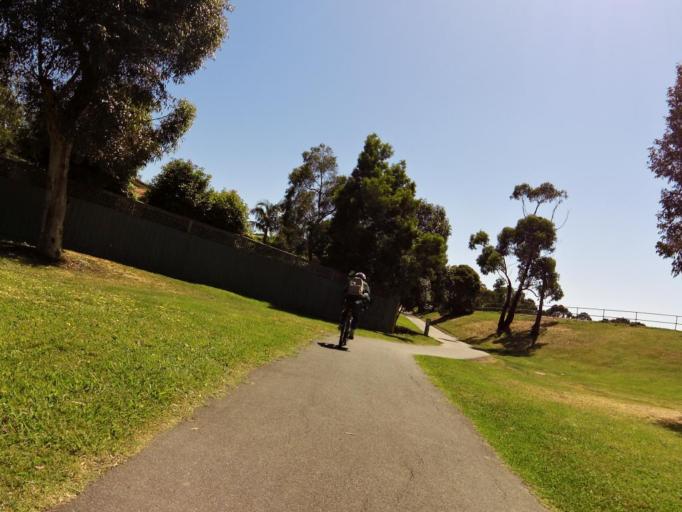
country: AU
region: Victoria
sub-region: Knox
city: Knoxfield
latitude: -37.8666
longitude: 145.2417
